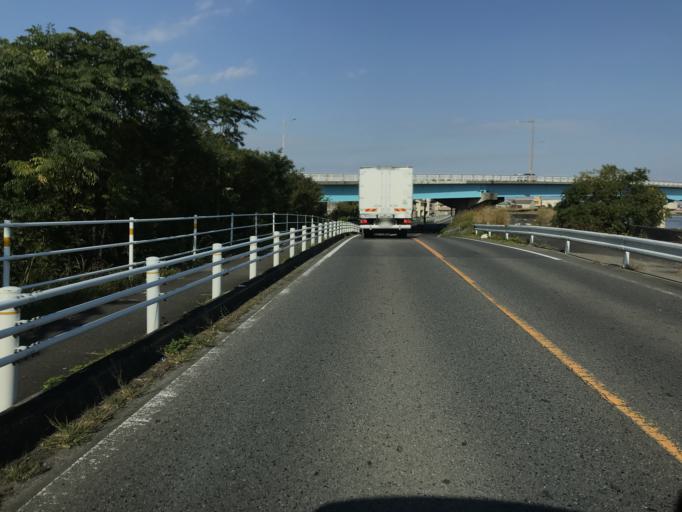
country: JP
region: Aichi
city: Kanie
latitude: 35.1682
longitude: 136.8268
